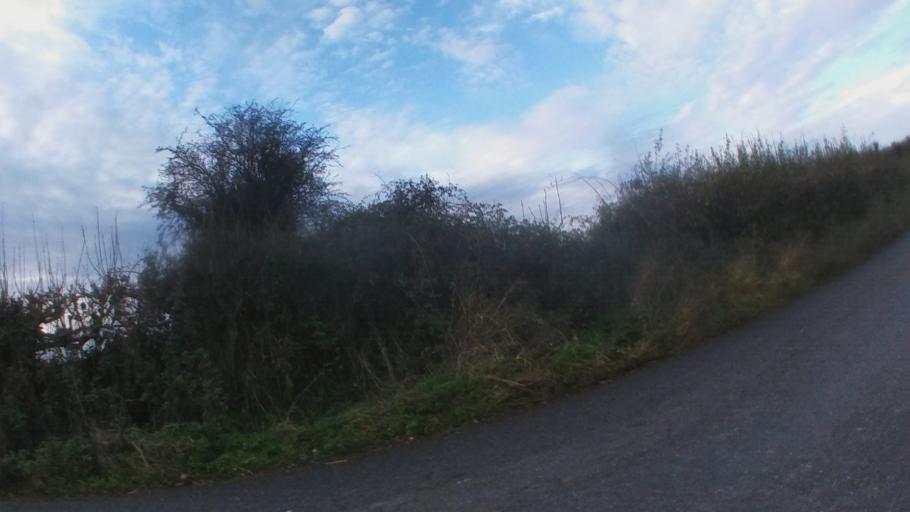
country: IE
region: Leinster
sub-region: Kilkenny
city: Kilkenny
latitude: 52.6857
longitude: -7.1759
